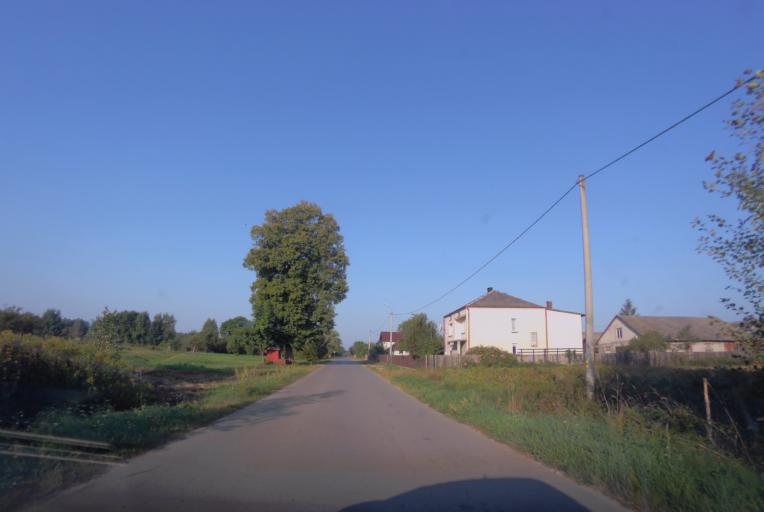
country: PL
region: Lublin Voivodeship
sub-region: Powiat janowski
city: Dzwola
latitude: 50.5790
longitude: 22.5504
